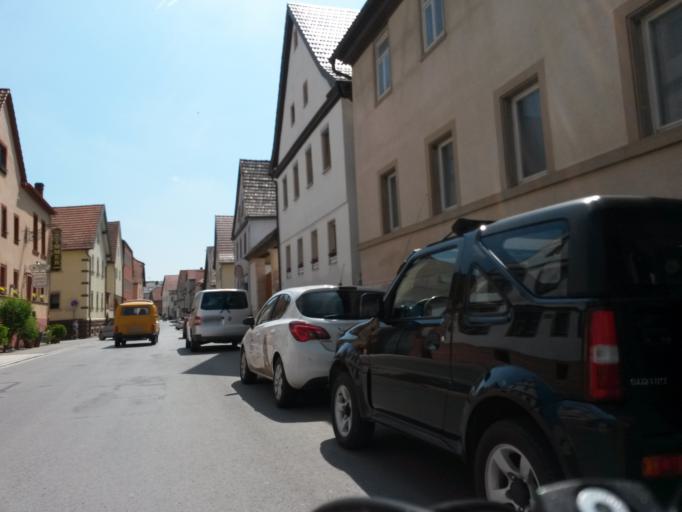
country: DE
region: Bavaria
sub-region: Regierungsbezirk Unterfranken
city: Elfershausen
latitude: 50.1467
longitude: 9.9616
